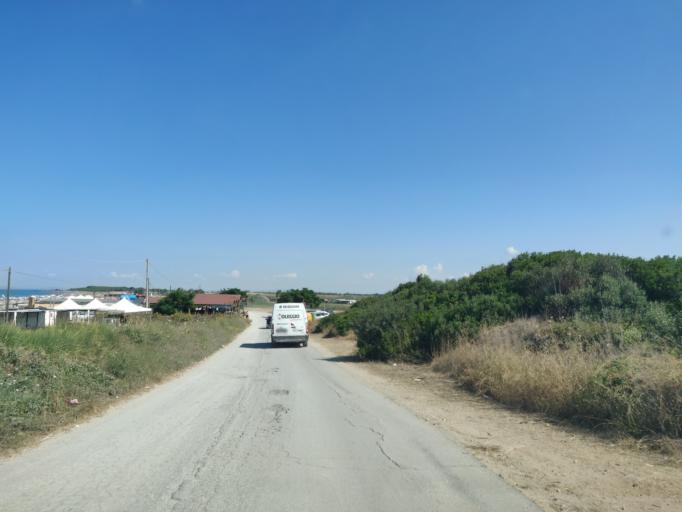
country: IT
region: Latium
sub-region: Citta metropolitana di Roma Capitale
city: Aurelia
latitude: 42.1707
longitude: 11.7410
